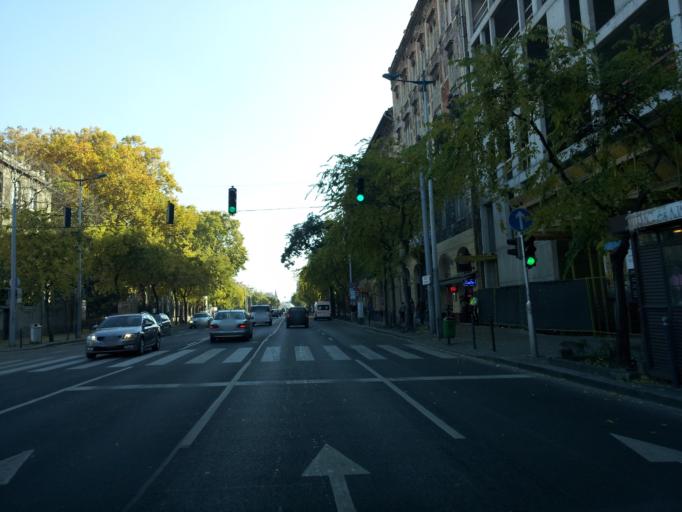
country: HU
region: Budapest
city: Budapest VIII. keruelet
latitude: 47.4826
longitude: 19.0791
